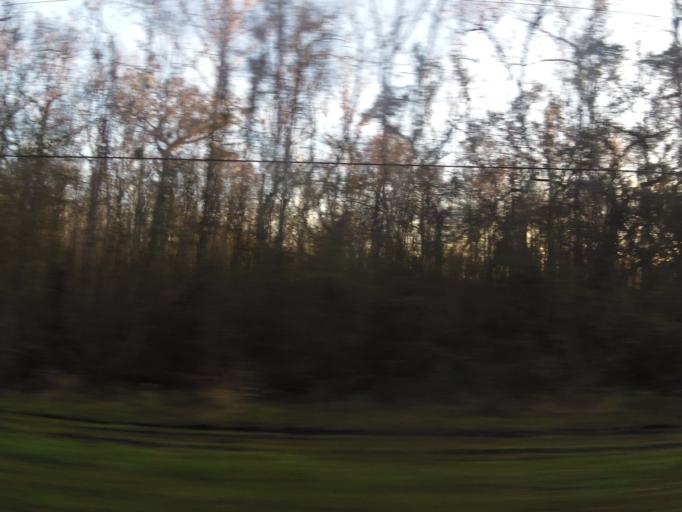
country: US
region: Florida
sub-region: Clay County
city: Green Cove Springs
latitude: 29.9268
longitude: -81.5815
